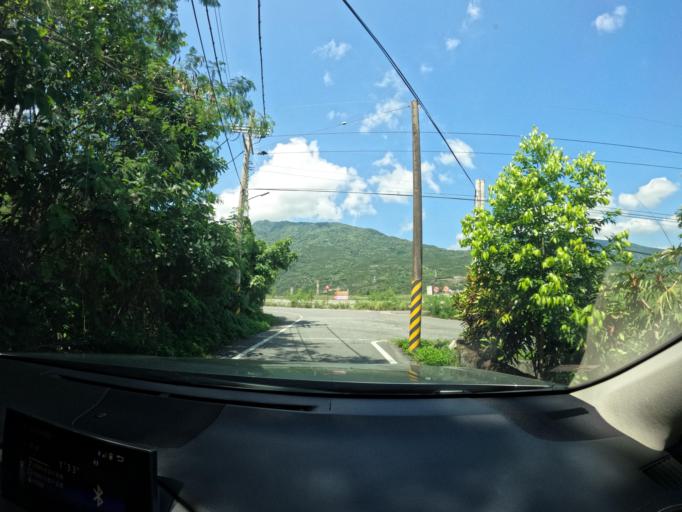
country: TW
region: Taiwan
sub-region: Hualien
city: Hualian
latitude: 23.6866
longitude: 121.4071
